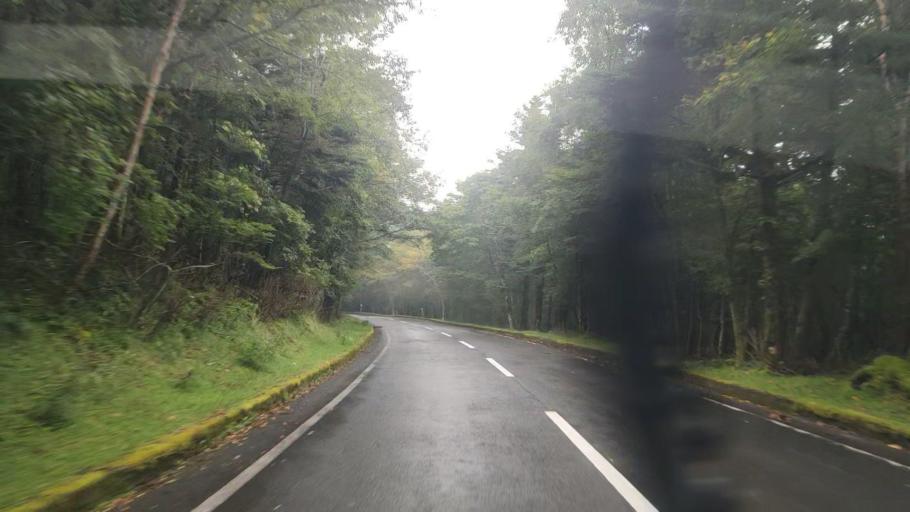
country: JP
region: Shizuoka
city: Fujinomiya
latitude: 35.3169
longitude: 138.7302
